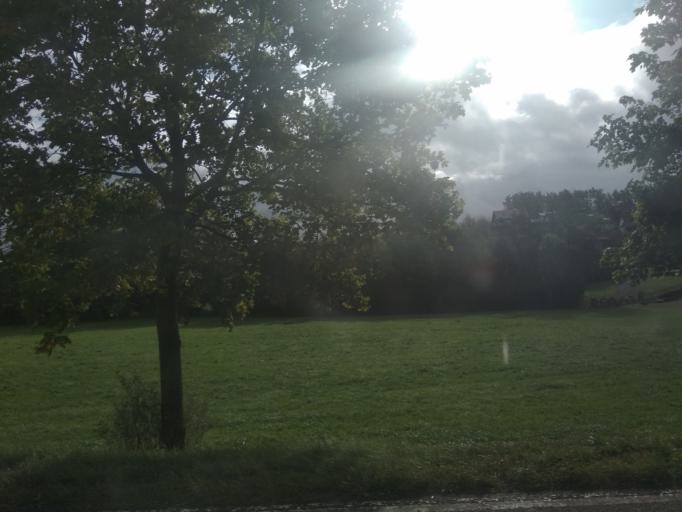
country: DE
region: Baden-Wuerttemberg
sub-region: Karlsruhe Region
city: Seckach
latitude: 49.4088
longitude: 9.2805
